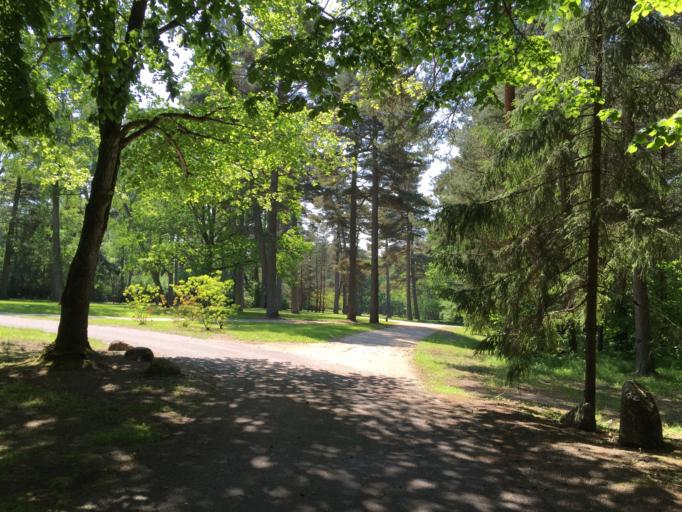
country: LT
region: Klaipedos apskritis
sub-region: Klaipeda
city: Palanga
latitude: 55.9040
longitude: 21.0594
